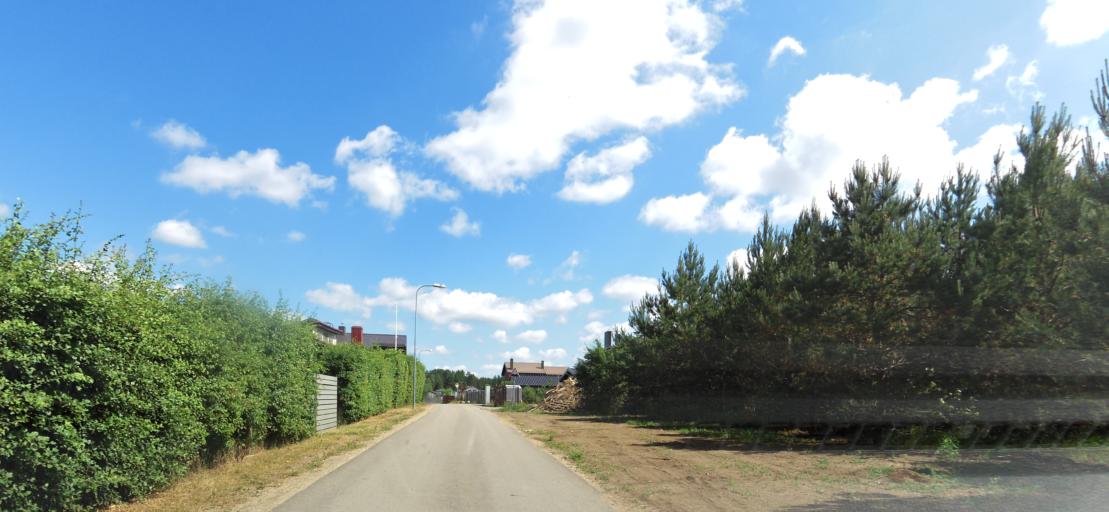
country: LT
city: Nemencine
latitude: 54.8199
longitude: 25.3939
